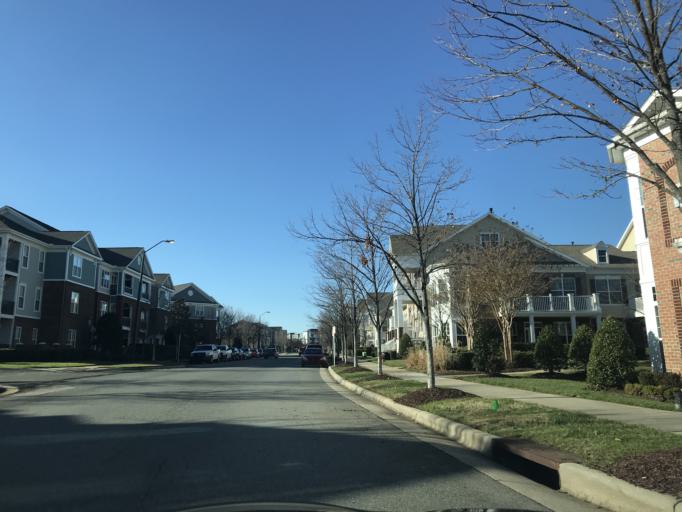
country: US
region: North Carolina
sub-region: Wake County
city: Morrisville
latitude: 35.8983
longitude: -78.7971
